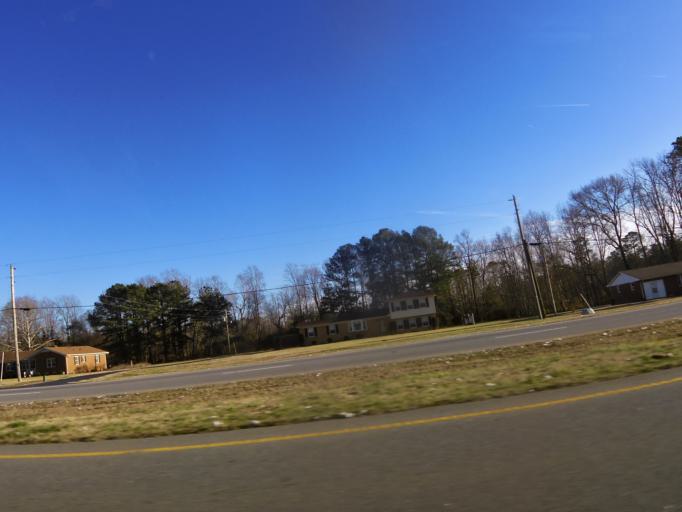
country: US
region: Virginia
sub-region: City of Franklin
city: Franklin
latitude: 36.6557
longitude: -76.8198
